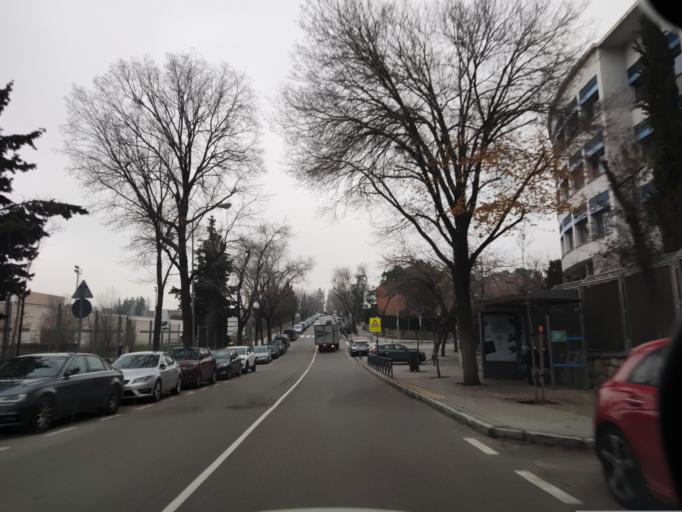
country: ES
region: Madrid
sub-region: Provincia de Madrid
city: Tetuan de las Victorias
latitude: 40.4839
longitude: -3.7142
